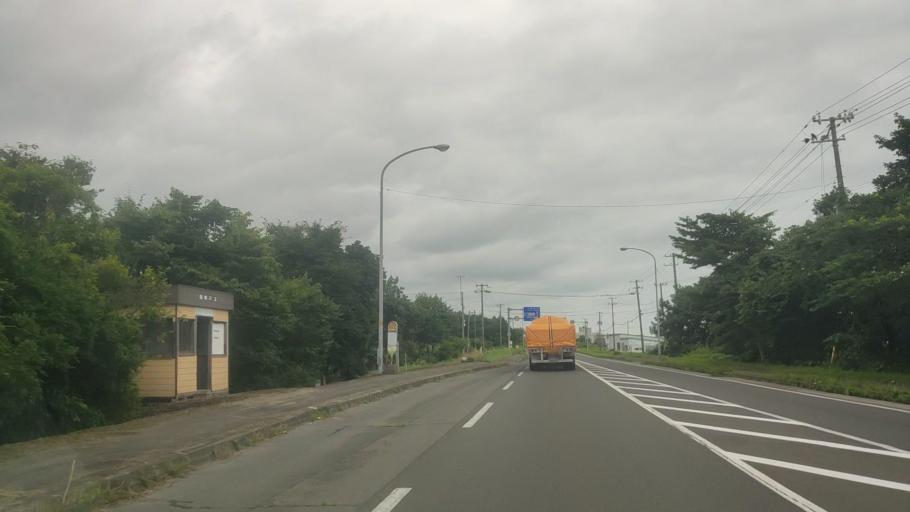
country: JP
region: Hokkaido
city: Shiraoi
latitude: 42.5246
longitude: 141.3156
